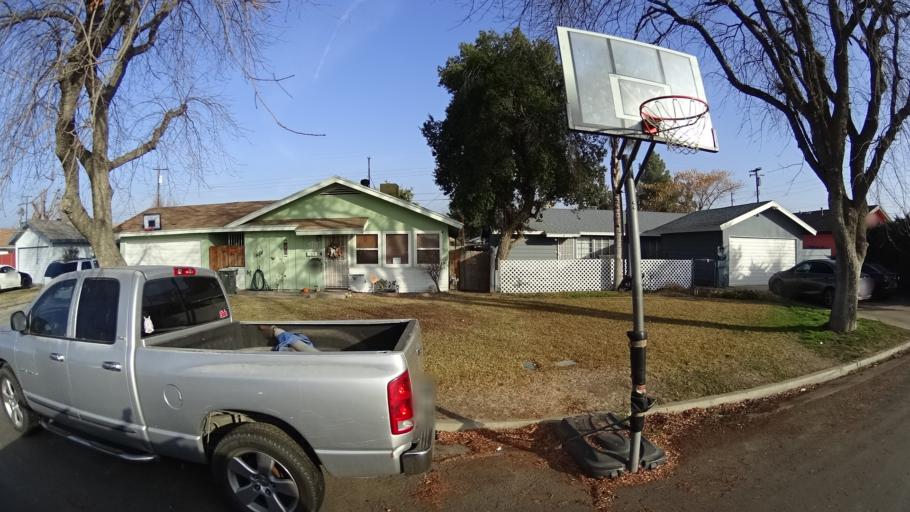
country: US
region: California
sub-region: Kern County
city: Bakersfield
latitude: 35.3339
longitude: -119.0220
